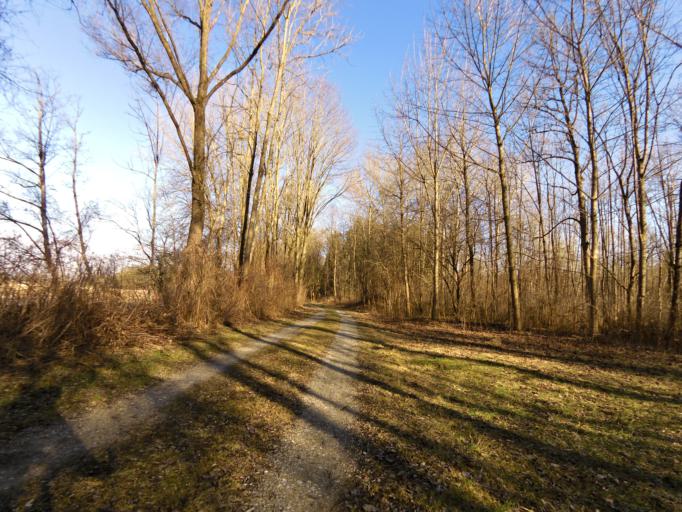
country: DE
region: Bavaria
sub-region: Lower Bavaria
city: Tiefenbach
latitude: 48.5180
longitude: 12.0967
